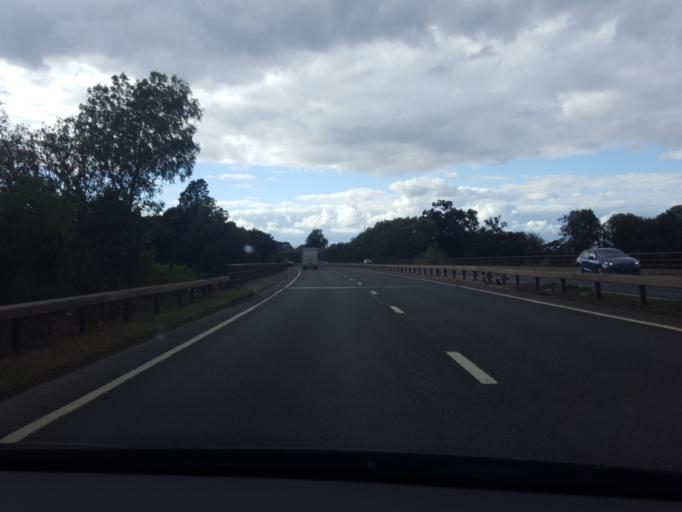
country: GB
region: England
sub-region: Leicestershire
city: Barrow upon Soar
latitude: 52.7473
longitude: -1.1568
